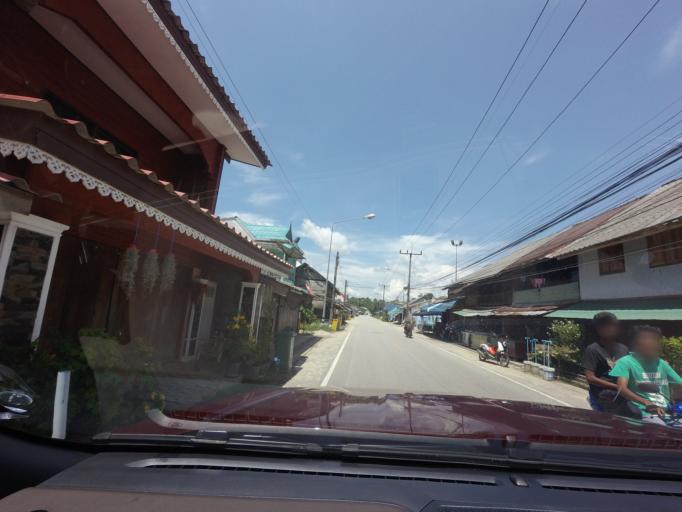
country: TH
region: Narathiwat
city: Chanae
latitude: 6.1288
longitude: 101.6981
